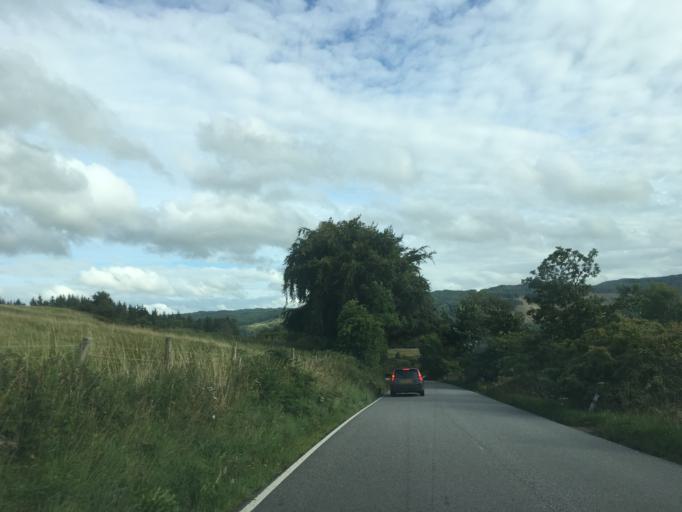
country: GB
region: Scotland
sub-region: Argyll and Bute
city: Oban
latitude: 56.3785
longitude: -5.4591
